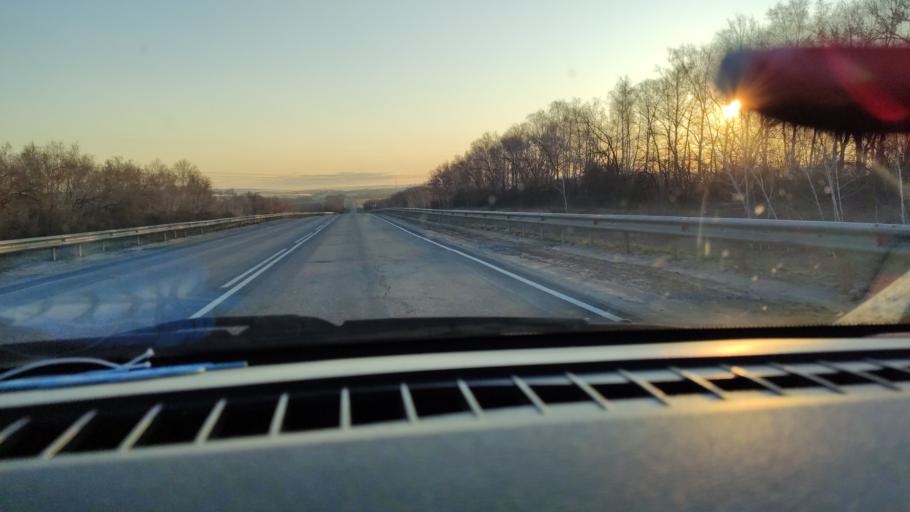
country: RU
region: Saratov
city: Sinodskoye
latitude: 51.9608
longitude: 46.6242
